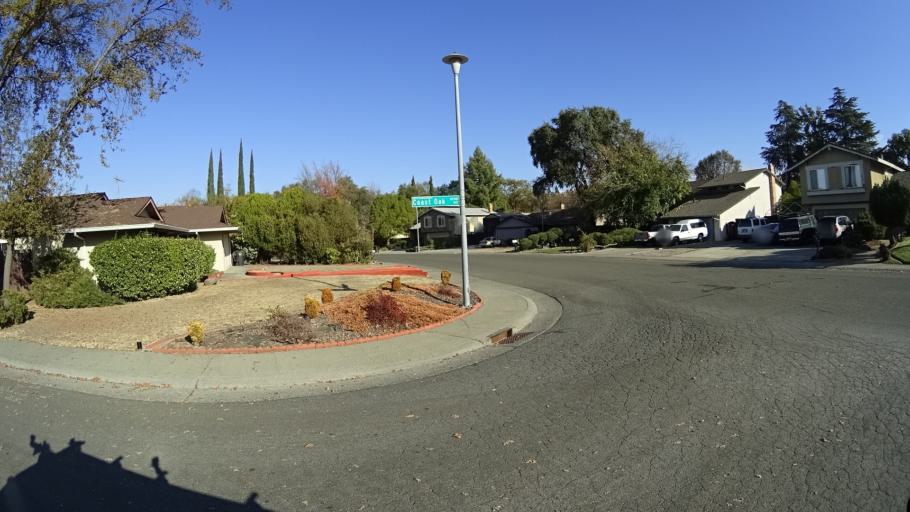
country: US
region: California
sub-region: Sacramento County
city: Citrus Heights
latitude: 38.7165
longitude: -121.2544
